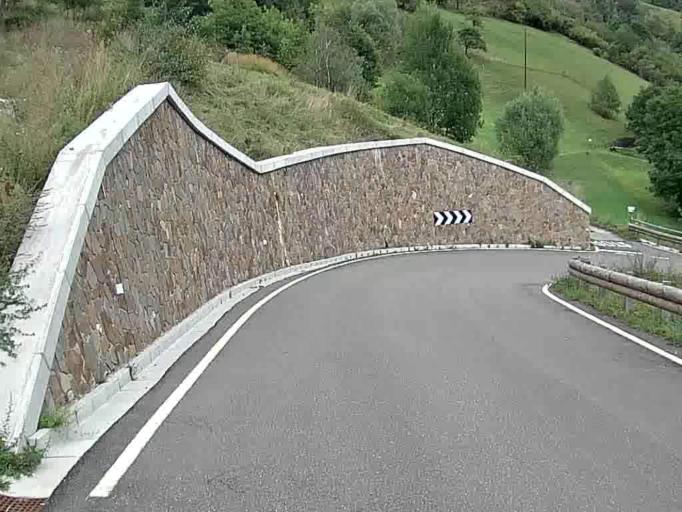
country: IT
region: Trentino-Alto Adige
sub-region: Provincia di Trento
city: Frassilongo
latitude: 46.0728
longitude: 11.3042
